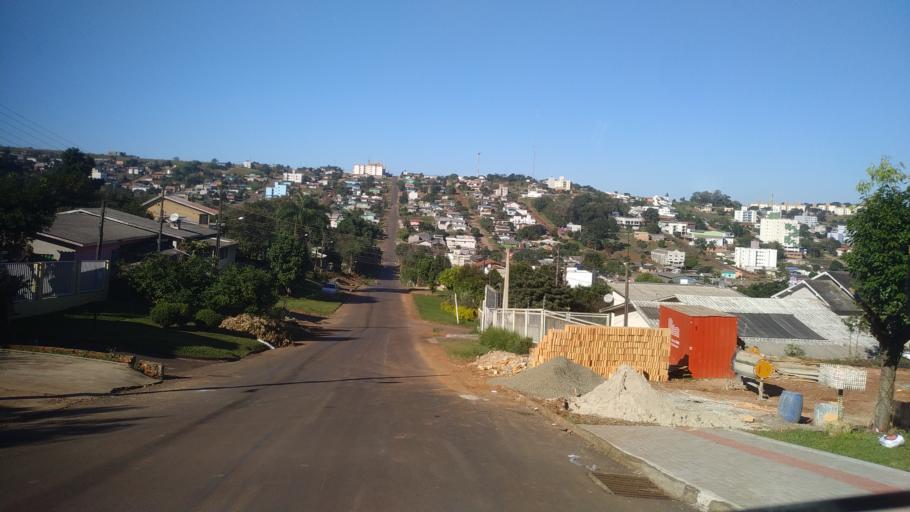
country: BR
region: Santa Catarina
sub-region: Chapeco
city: Chapeco
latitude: -27.1117
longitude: -52.5957
